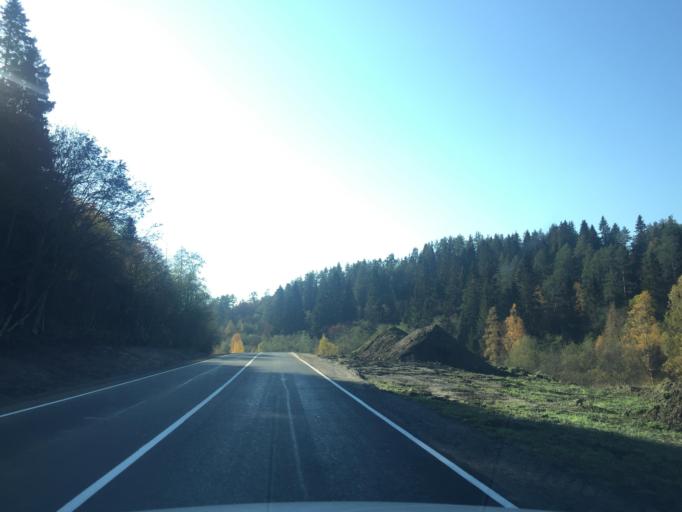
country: RU
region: Leningrad
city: Kuznechnoye
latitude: 61.3120
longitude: 29.8762
